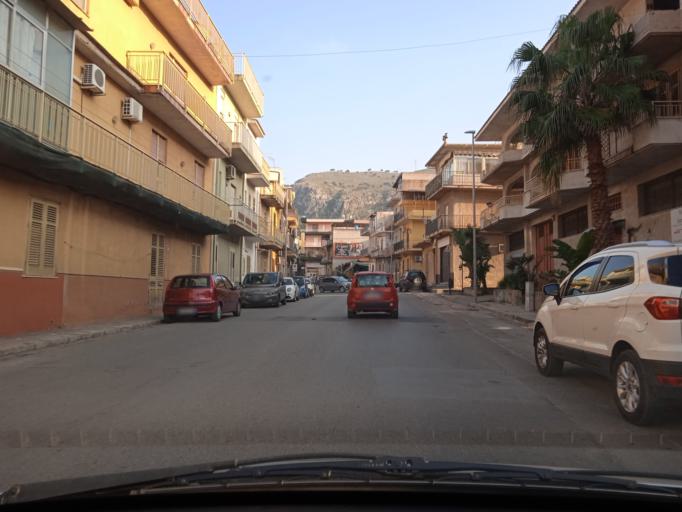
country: IT
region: Sicily
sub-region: Palermo
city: Villabate
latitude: 38.0770
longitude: 13.4390
